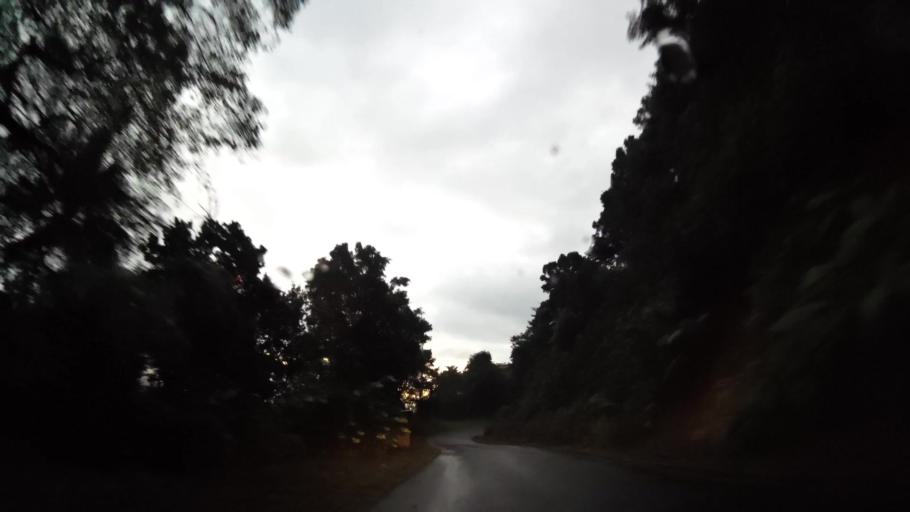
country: DM
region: Saint Andrew
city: Calibishie
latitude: 15.5871
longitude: -61.3309
